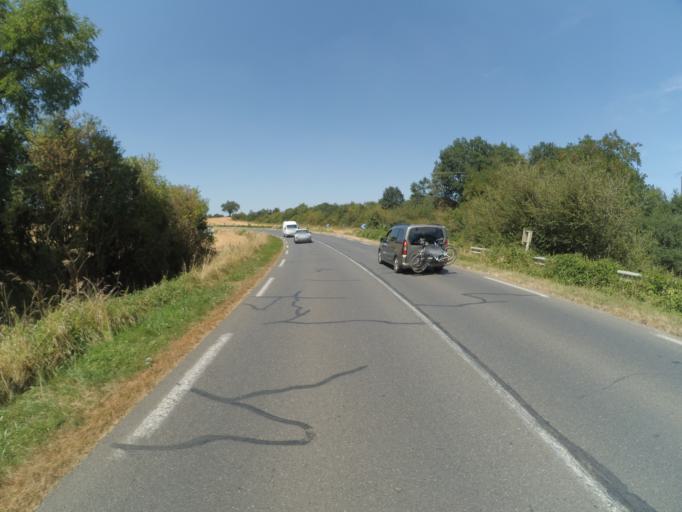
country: FR
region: Poitou-Charentes
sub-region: Departement de la Vienne
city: Lusignan
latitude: 46.4317
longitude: 0.1070
